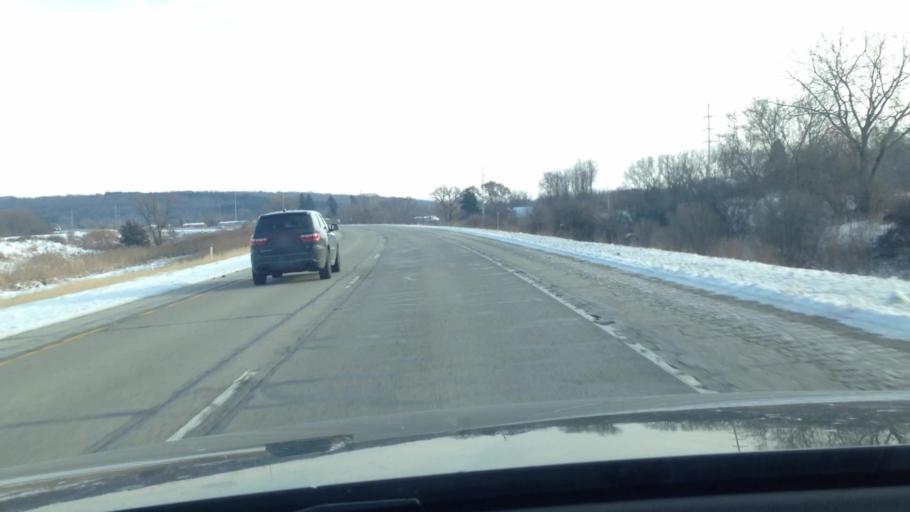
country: US
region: Wisconsin
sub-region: Walworth County
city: Como
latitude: 42.6186
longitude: -88.4598
